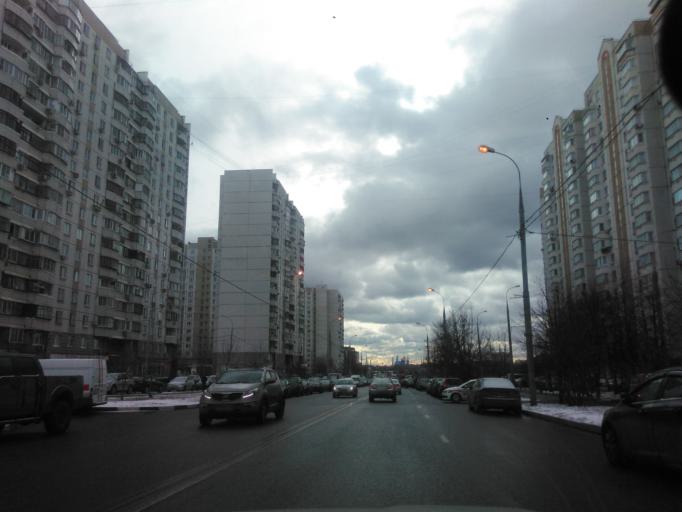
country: RU
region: Moskovskaya
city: Pavshino
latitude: 55.8441
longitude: 37.3505
